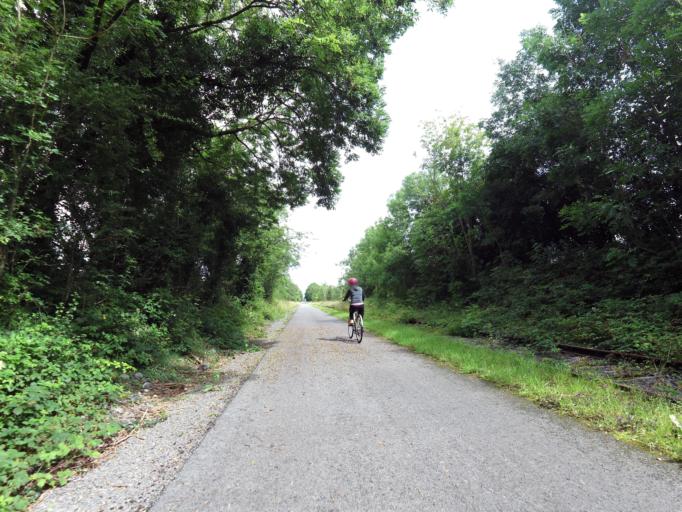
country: IE
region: Leinster
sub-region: An Iarmhi
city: Kilbeggan
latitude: 53.4753
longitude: -7.4835
